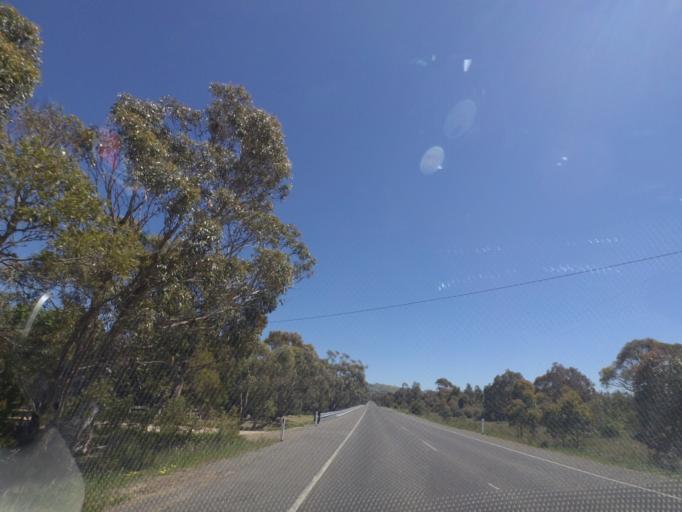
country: AU
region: Victoria
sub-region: Hume
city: Sunbury
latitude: -37.3055
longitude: 144.8361
